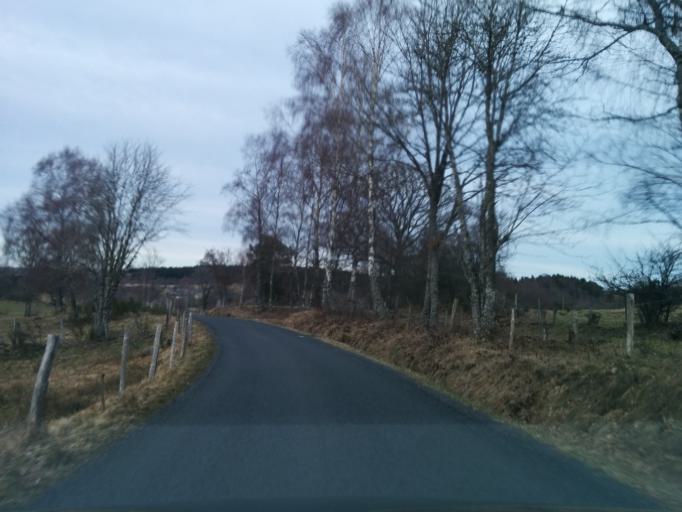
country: FR
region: Auvergne
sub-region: Departement du Cantal
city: Pierrefort
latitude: 44.8167
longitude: 2.8916
